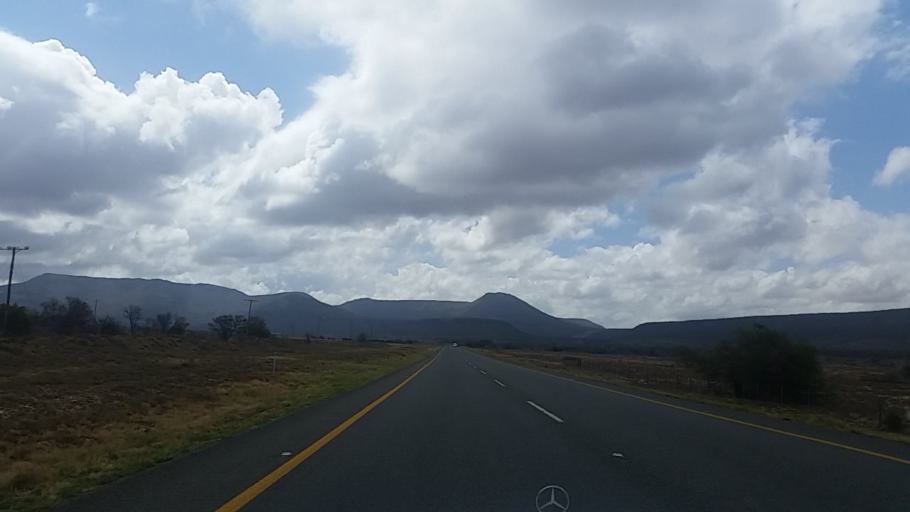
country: ZA
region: Eastern Cape
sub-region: Cacadu District Municipality
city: Graaff-Reinet
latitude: -32.0969
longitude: 24.6046
